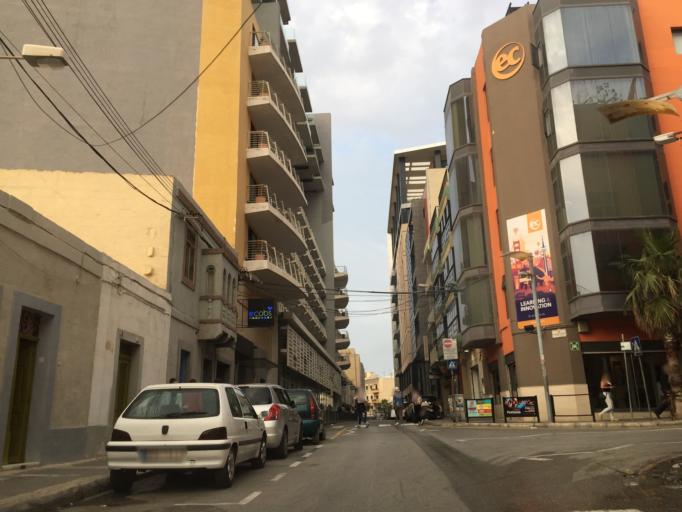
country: MT
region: Saint Julian
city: San Giljan
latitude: 35.9228
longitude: 14.4880
